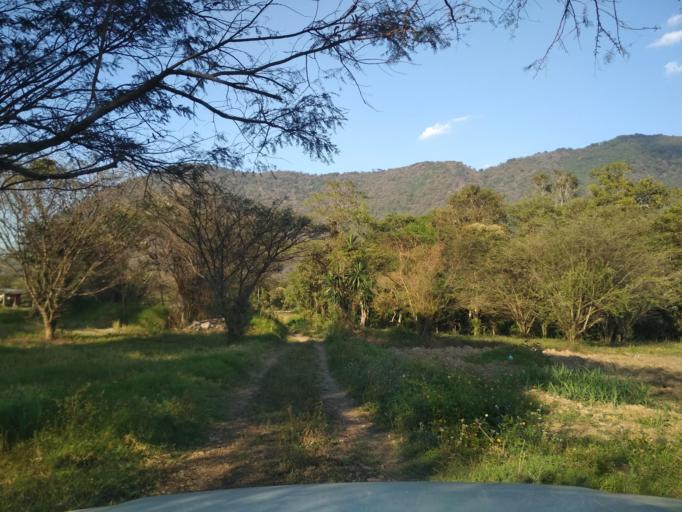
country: MX
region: Veracruz
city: Jalapilla
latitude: 18.8186
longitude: -97.0720
